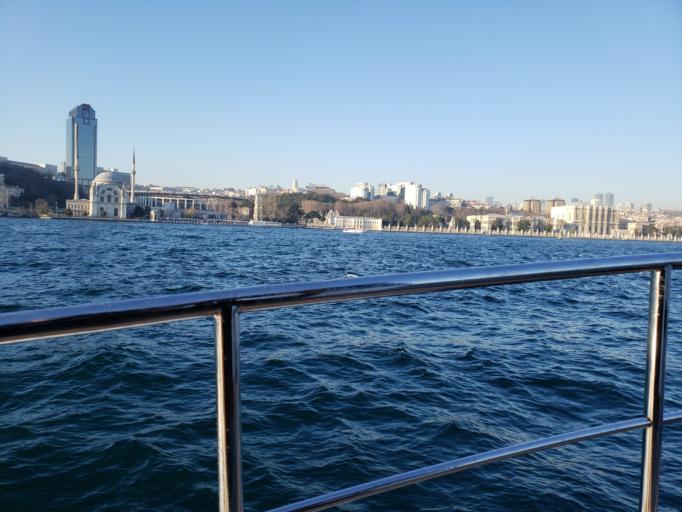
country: TR
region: Istanbul
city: UEskuedar
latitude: 41.0332
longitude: 28.9978
